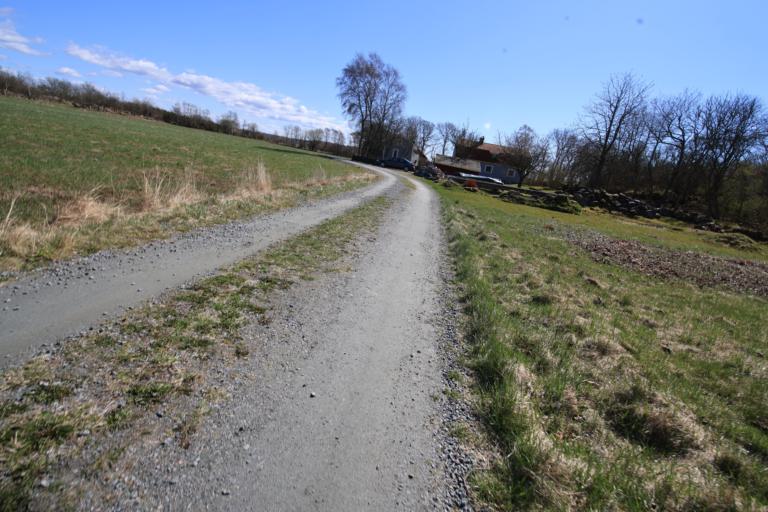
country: SE
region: Halland
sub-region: Varbergs Kommun
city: Varberg
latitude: 57.1610
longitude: 12.2515
